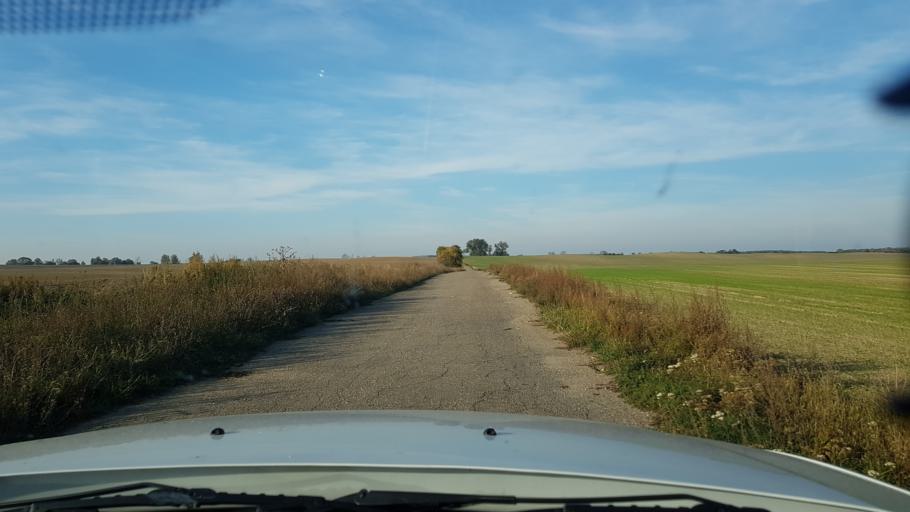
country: PL
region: West Pomeranian Voivodeship
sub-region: Powiat gryfinski
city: Moryn
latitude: 52.8804
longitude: 14.3114
